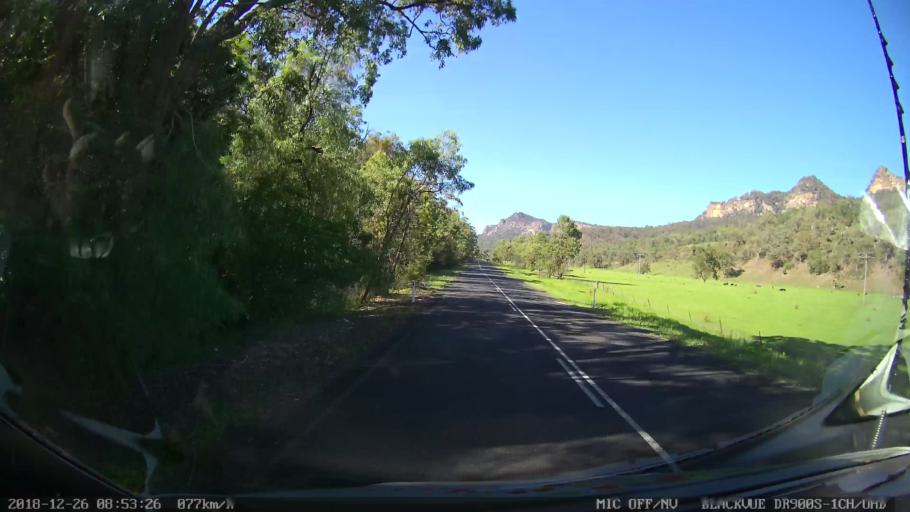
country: AU
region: New South Wales
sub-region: Mid-Western Regional
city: Kandos
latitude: -32.6042
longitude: 150.0775
